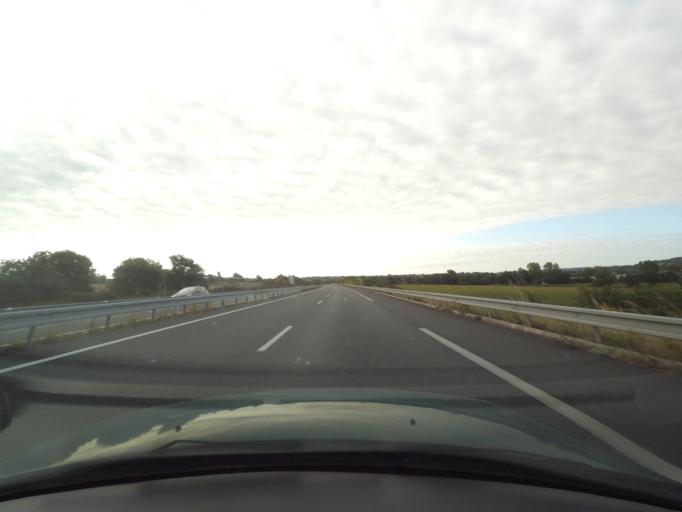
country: FR
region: Poitou-Charentes
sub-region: Departement des Deux-Sevres
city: Saint-Pierre-des-Echaubrognes
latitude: 46.9650
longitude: -0.7950
